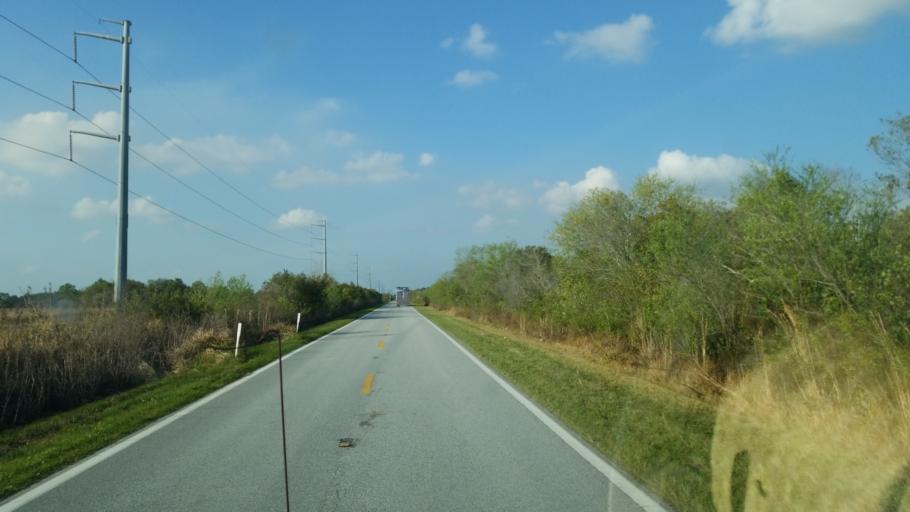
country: US
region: Florida
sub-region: Hardee County
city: Bowling Green
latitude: 27.6649
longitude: -81.9523
